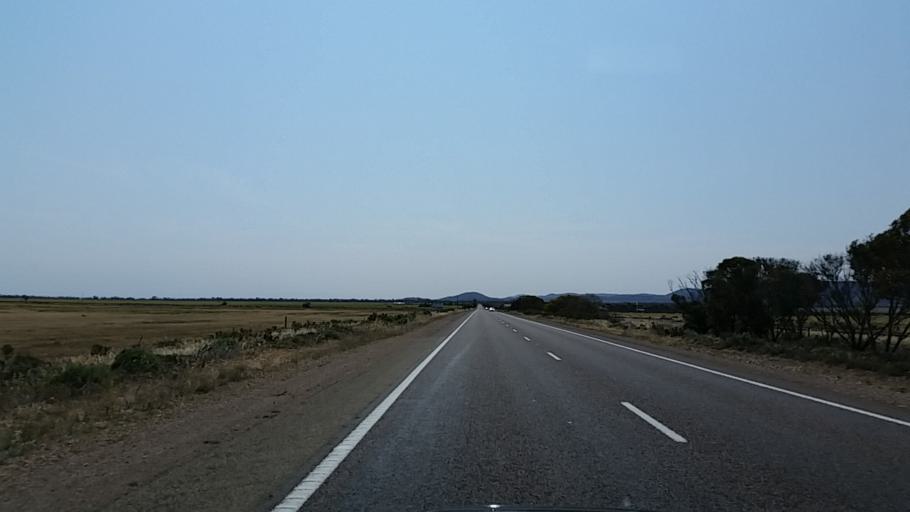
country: AU
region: South Australia
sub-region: Port Pirie City and Dists
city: Port Pirie
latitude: -32.8962
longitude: 137.9823
